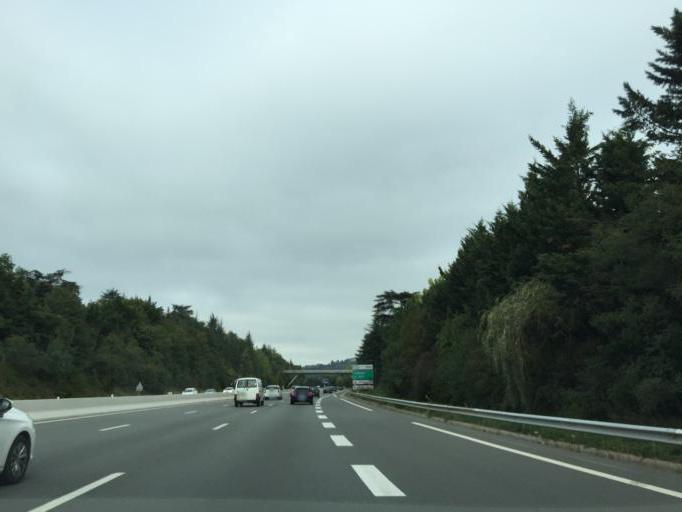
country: FR
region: Rhone-Alpes
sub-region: Departement de la Loire
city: Saint-Priest-en-Jarez
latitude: 45.4703
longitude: 4.3658
